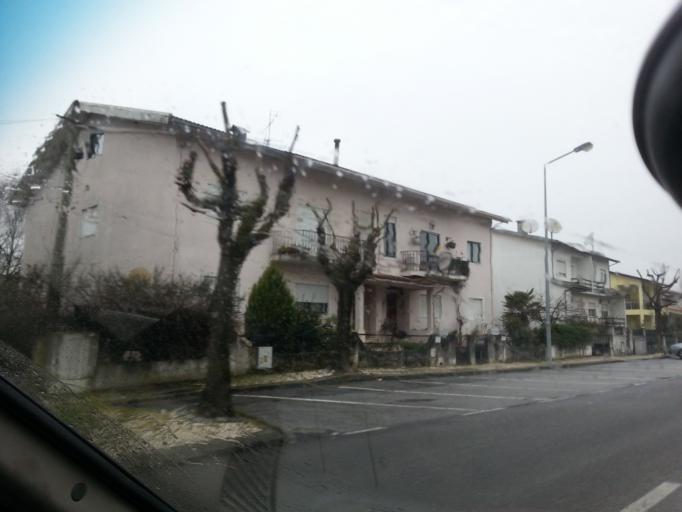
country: PT
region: Viseu
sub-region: Viseu
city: Rio de Loba
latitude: 40.6673
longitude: -7.8814
